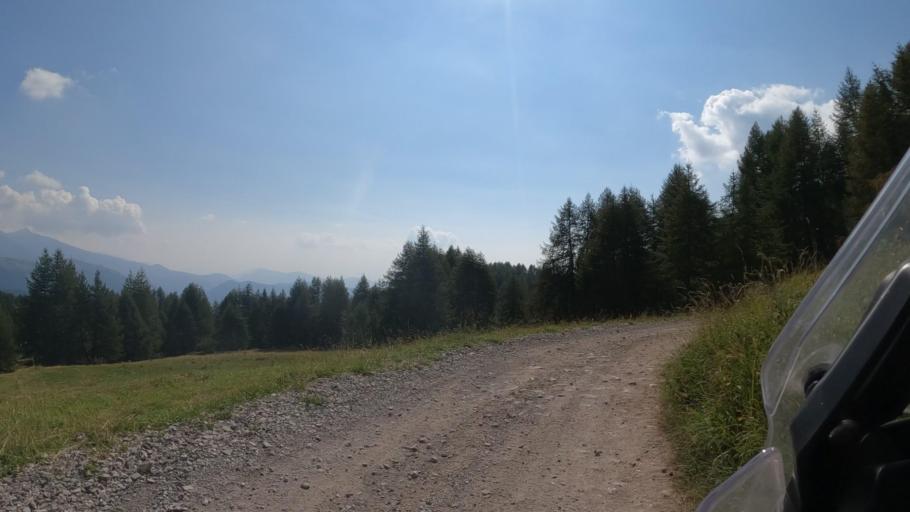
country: IT
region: Piedmont
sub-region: Provincia di Cuneo
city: Briga Alta
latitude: 44.0898
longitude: 7.7216
